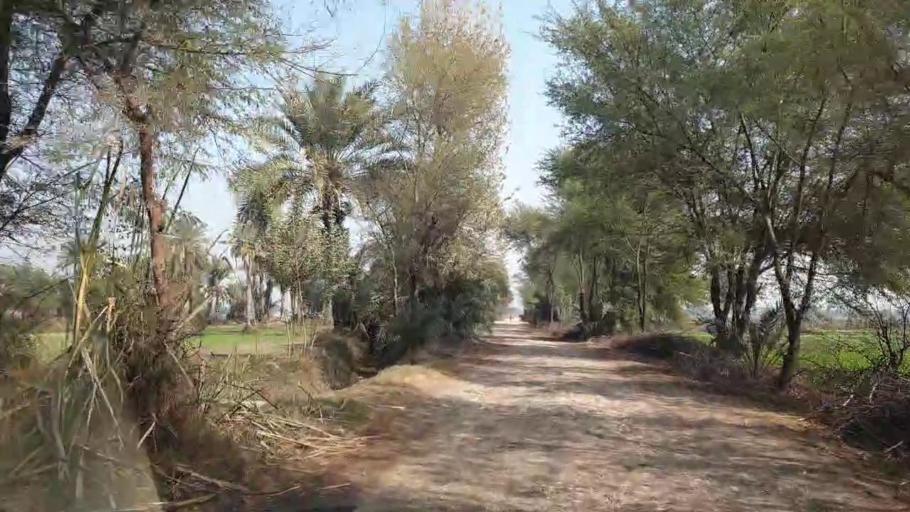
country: PK
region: Sindh
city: Ubauro
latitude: 28.1132
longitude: 69.7763
